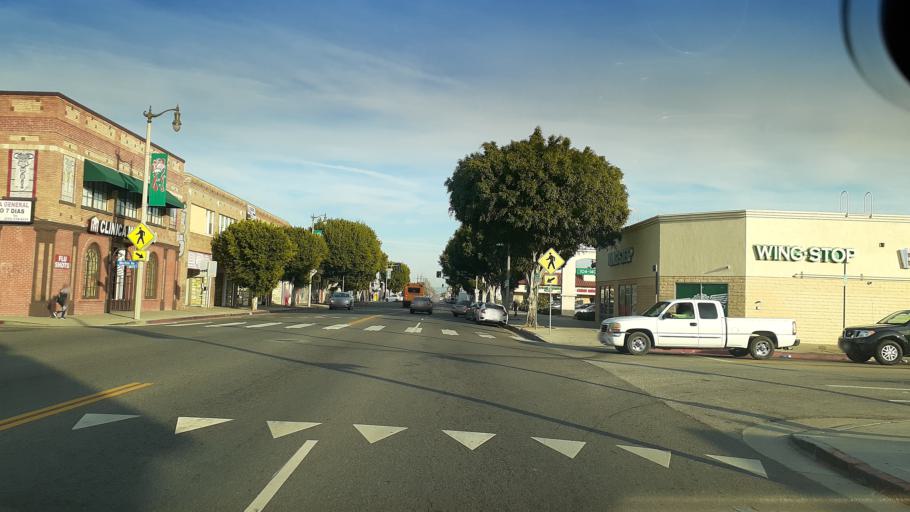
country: US
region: California
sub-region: Los Angeles County
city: West Carson
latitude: 33.7799
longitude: -118.2640
